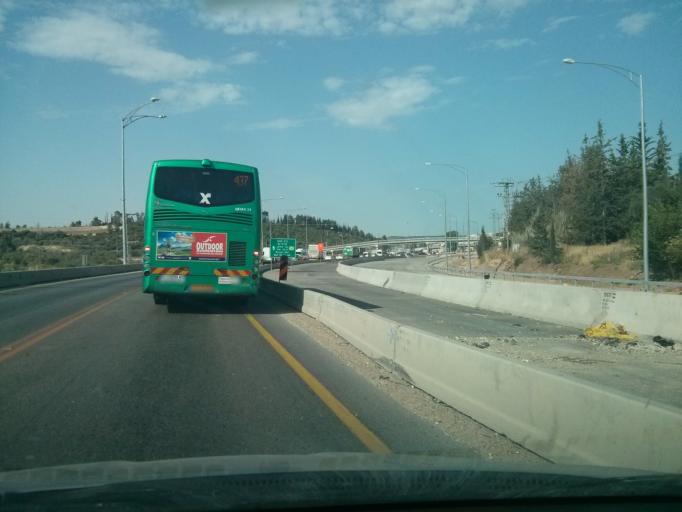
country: IL
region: Jerusalem
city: Bet Shemesh
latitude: 31.7792
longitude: 35.0136
